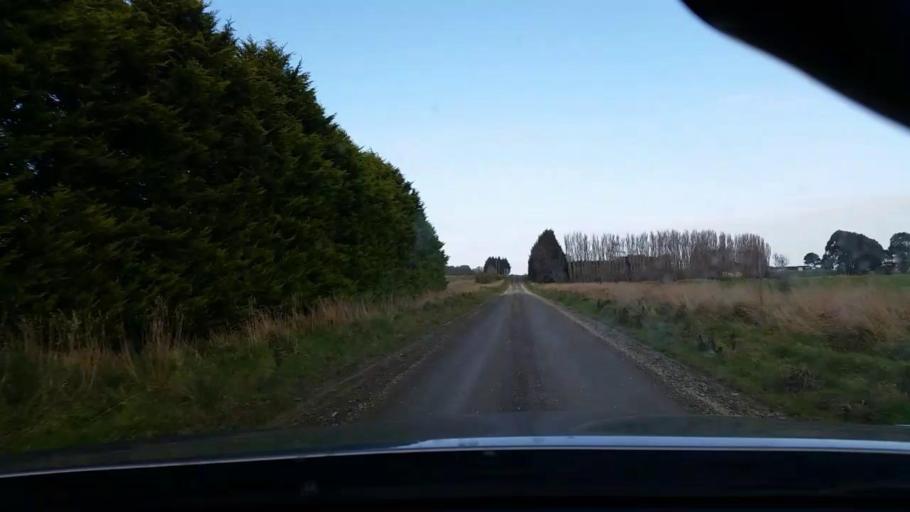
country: NZ
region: Southland
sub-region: Southland District
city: Winton
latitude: -46.2747
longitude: 168.2924
